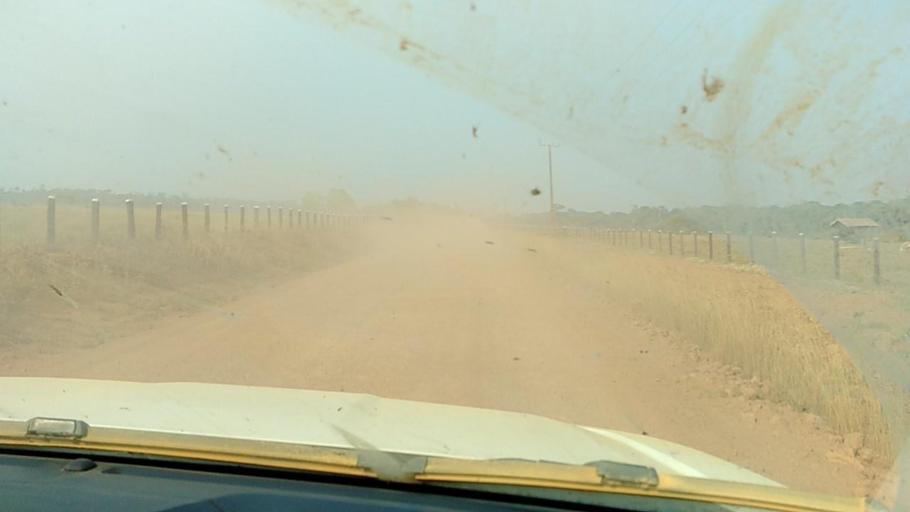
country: BR
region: Rondonia
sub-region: Porto Velho
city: Porto Velho
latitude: -8.7787
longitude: -64.0852
